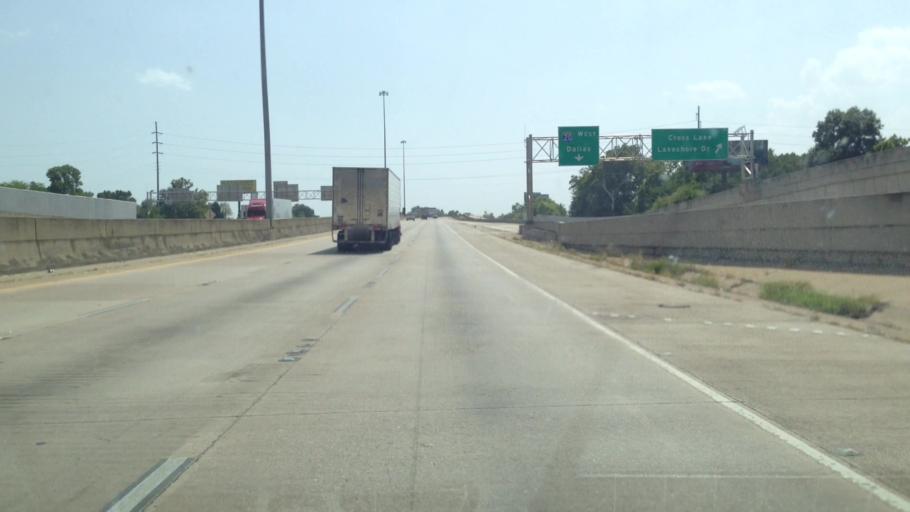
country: US
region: Louisiana
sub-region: Caddo Parish
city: Shreveport
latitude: 32.4947
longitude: -93.7647
